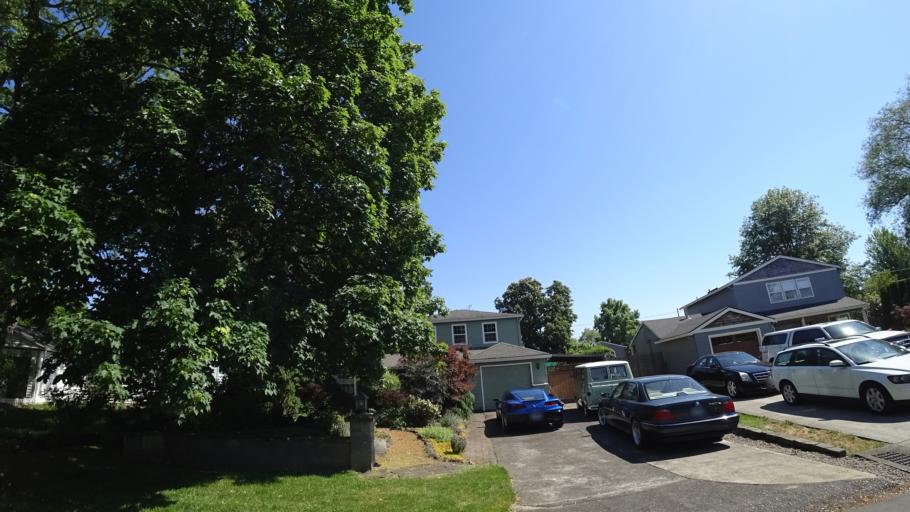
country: US
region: Oregon
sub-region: Washington County
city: Cedar Hills
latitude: 45.4971
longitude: -122.7993
